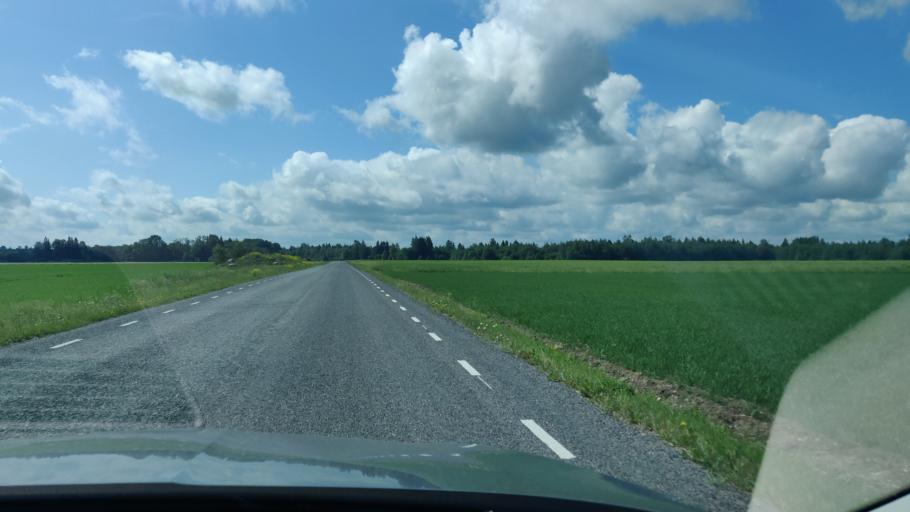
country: EE
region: Jaervamaa
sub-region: Paide linn
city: Paide
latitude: 58.8638
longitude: 25.6650
